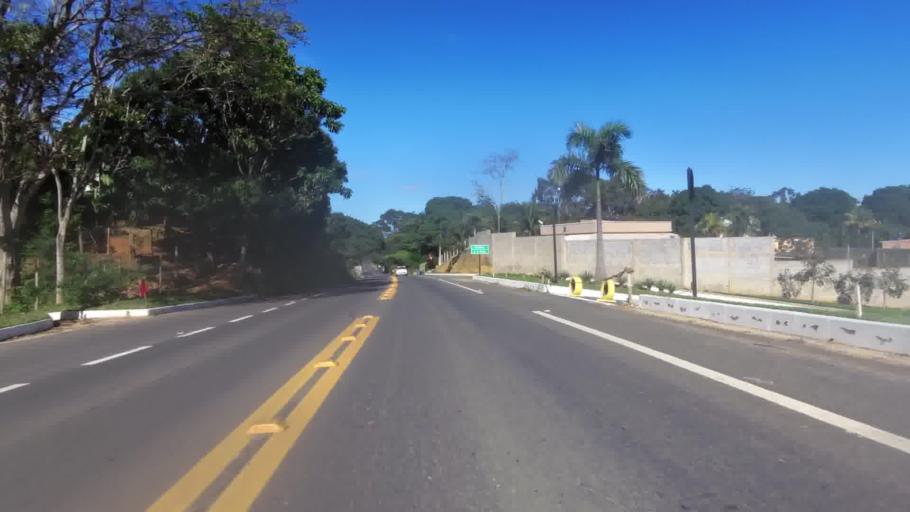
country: BR
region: Espirito Santo
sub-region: Piuma
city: Piuma
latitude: -20.8162
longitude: -40.6893
